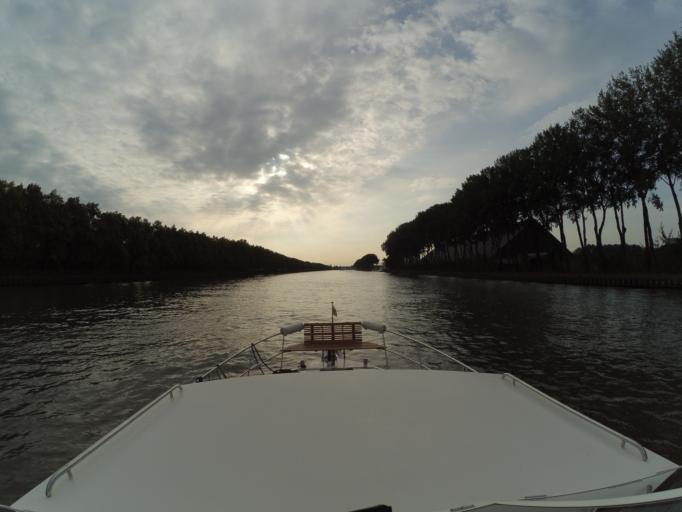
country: NL
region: Utrecht
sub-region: Stichtse Vecht
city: Maarssen
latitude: 52.1220
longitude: 5.0616
